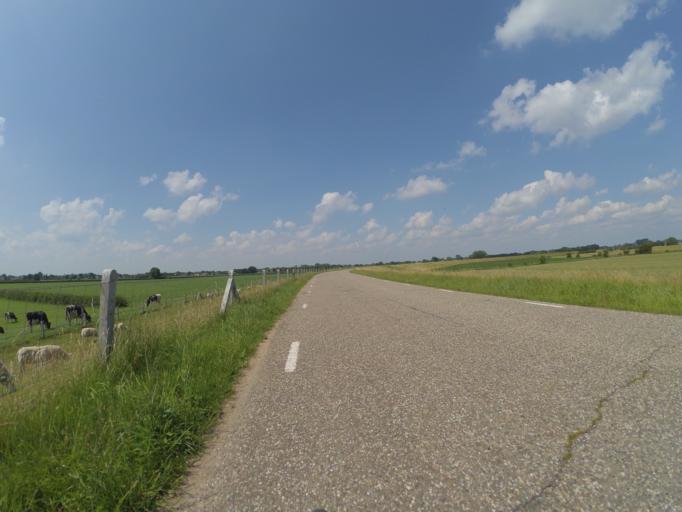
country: NL
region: Utrecht
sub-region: Gemeente Wijk bij Duurstede
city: Wijk bij Duurstede
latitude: 51.9515
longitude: 5.3163
